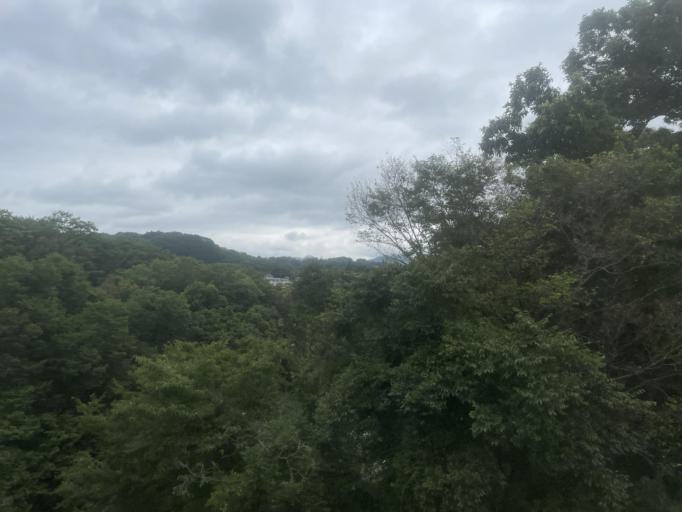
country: JP
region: Saitama
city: Chichibu
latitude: 36.0437
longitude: 139.1009
